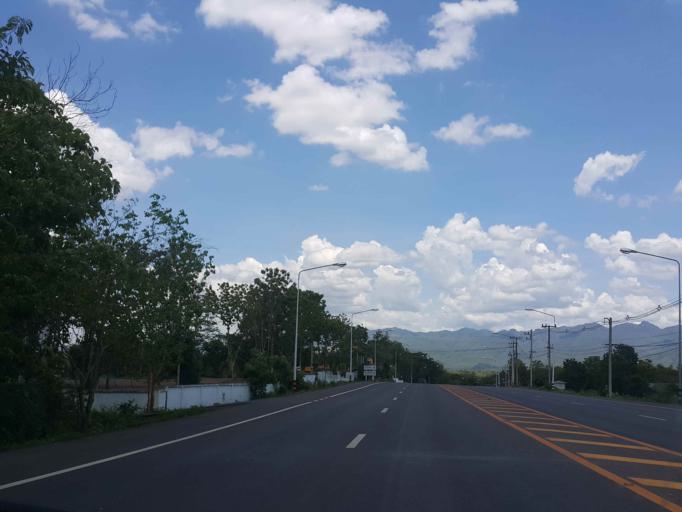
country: TH
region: Phrae
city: Nong Muang Khai
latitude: 18.2013
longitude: 100.2222
